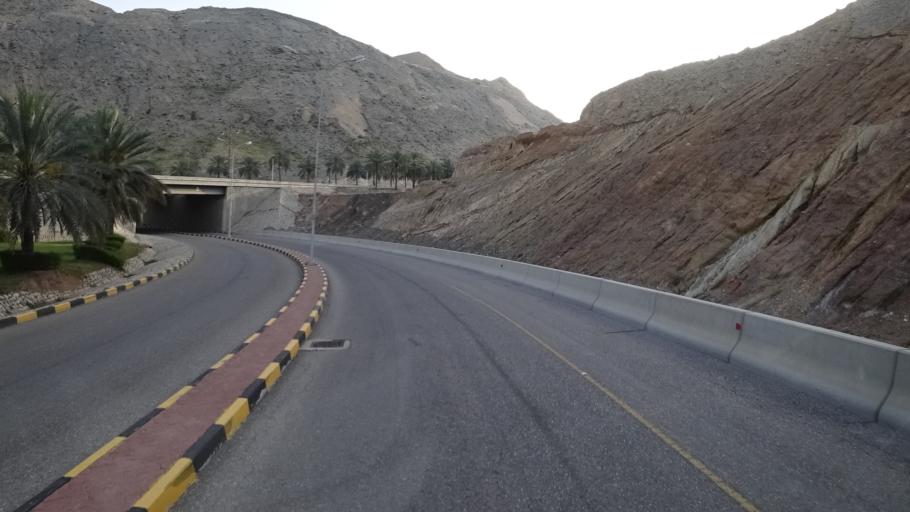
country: OM
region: Muhafazat Masqat
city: Muscat
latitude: 23.5603
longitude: 58.5941
